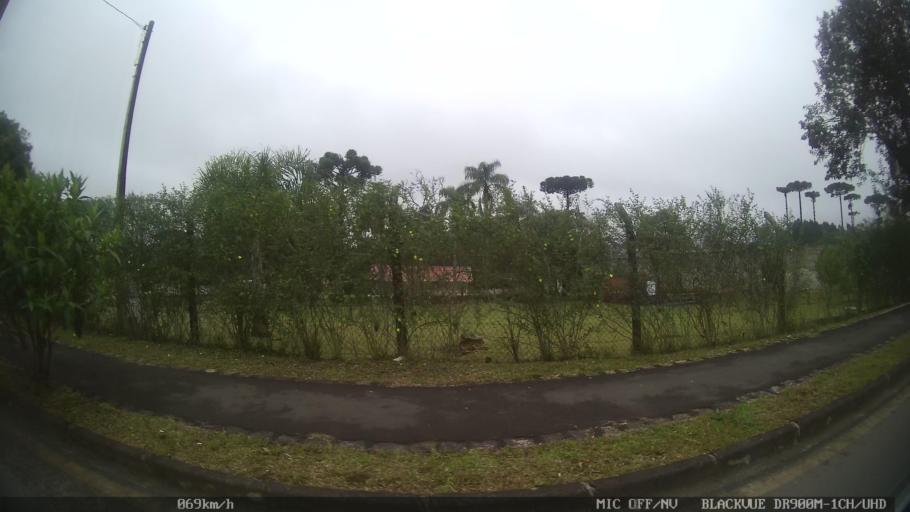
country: BR
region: Parana
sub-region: Sao Jose Dos Pinhais
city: Sao Jose dos Pinhais
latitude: -25.5742
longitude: -49.1709
